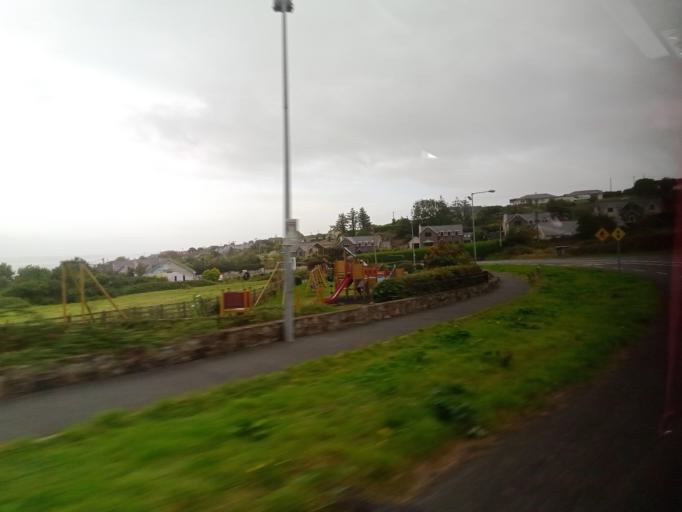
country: IE
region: Munster
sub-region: Waterford
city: Dungarvan
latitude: 52.0458
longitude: -7.5688
